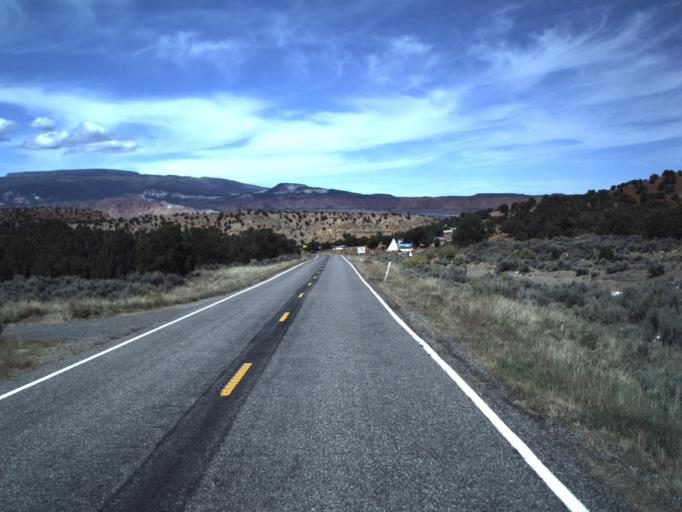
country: US
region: Utah
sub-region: Wayne County
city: Loa
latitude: 38.2474
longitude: -111.3773
